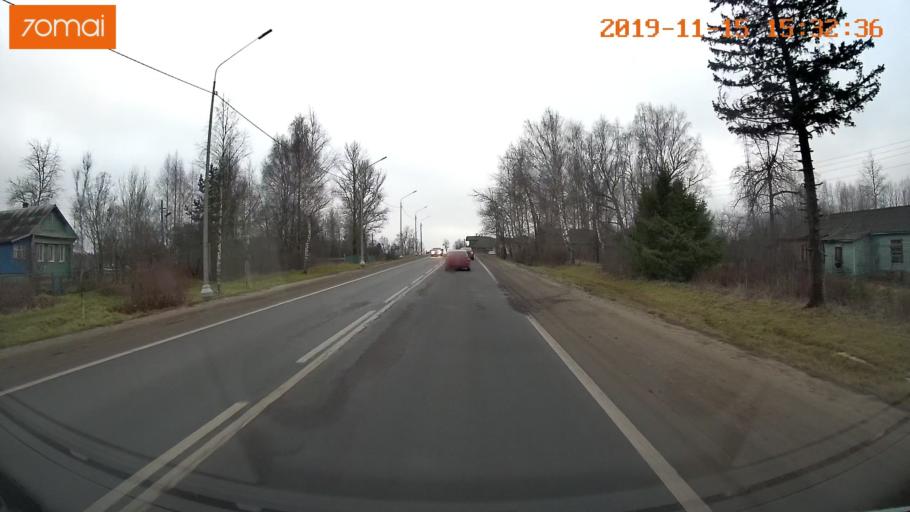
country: RU
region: Jaroslavl
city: Danilov
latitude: 58.0887
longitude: 40.0984
